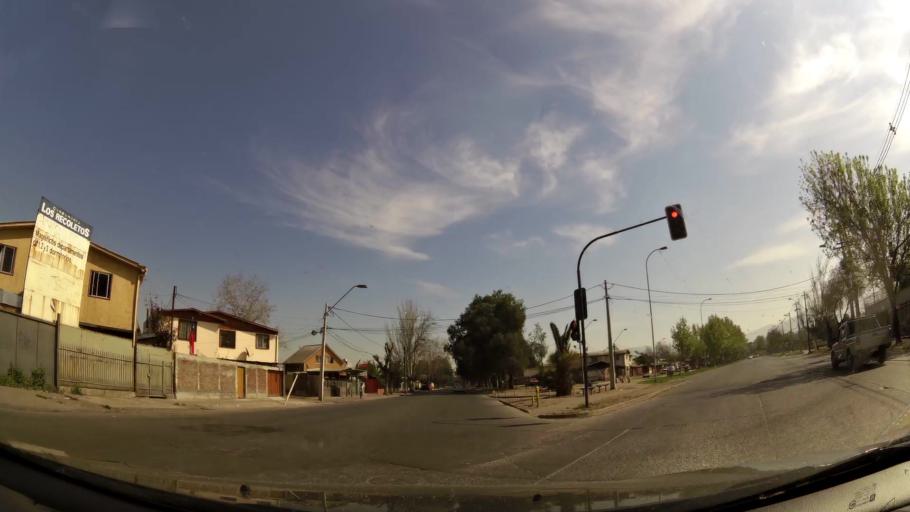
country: CL
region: Santiago Metropolitan
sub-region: Provincia de Santiago
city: Santiago
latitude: -33.3918
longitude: -70.6573
